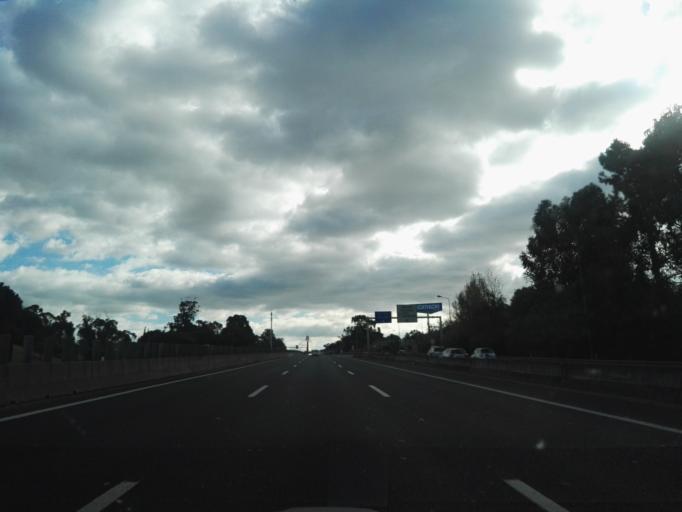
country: PT
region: Setubal
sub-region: Almada
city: Pragal
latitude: 38.6612
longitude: -9.1709
